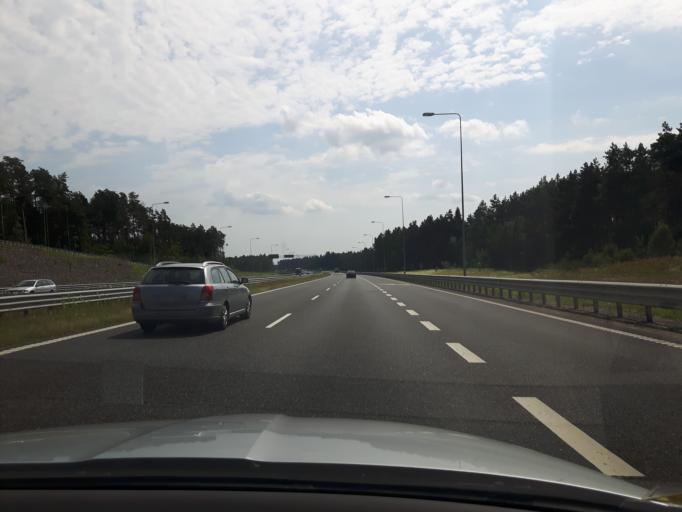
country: PL
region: Warmian-Masurian Voivodeship
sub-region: Powiat olsztynski
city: Olsztynek
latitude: 53.5306
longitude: 20.2774
